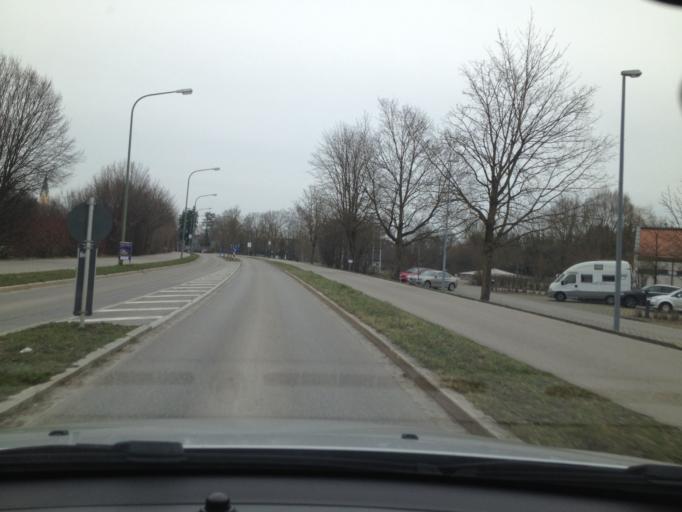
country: DE
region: Bavaria
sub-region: Swabia
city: Bobingen
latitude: 48.2692
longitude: 10.8234
